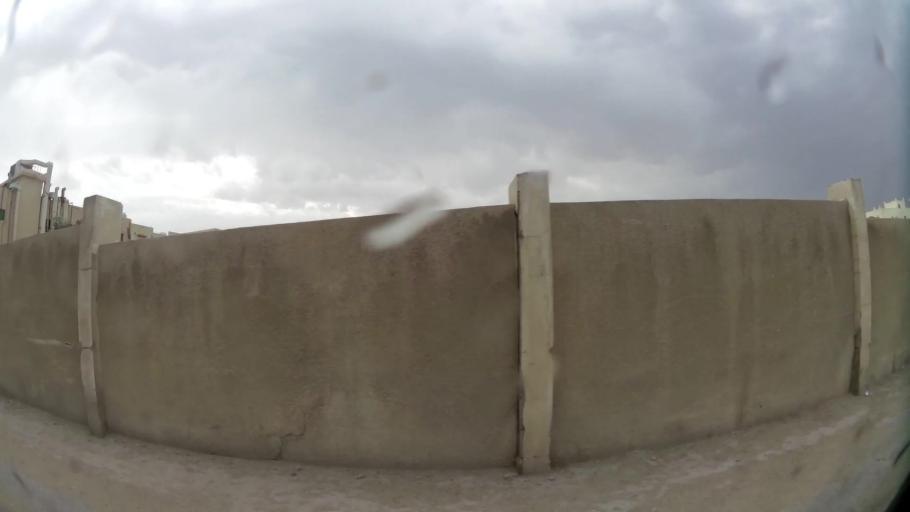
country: QA
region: Baladiyat ad Dawhah
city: Doha
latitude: 25.2741
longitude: 51.4963
